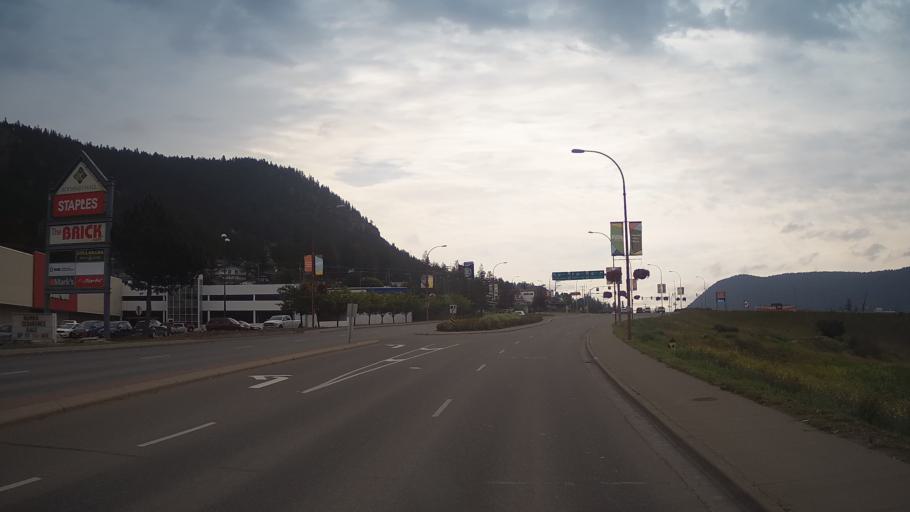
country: CA
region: British Columbia
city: Williams Lake
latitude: 52.1283
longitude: -122.1320
